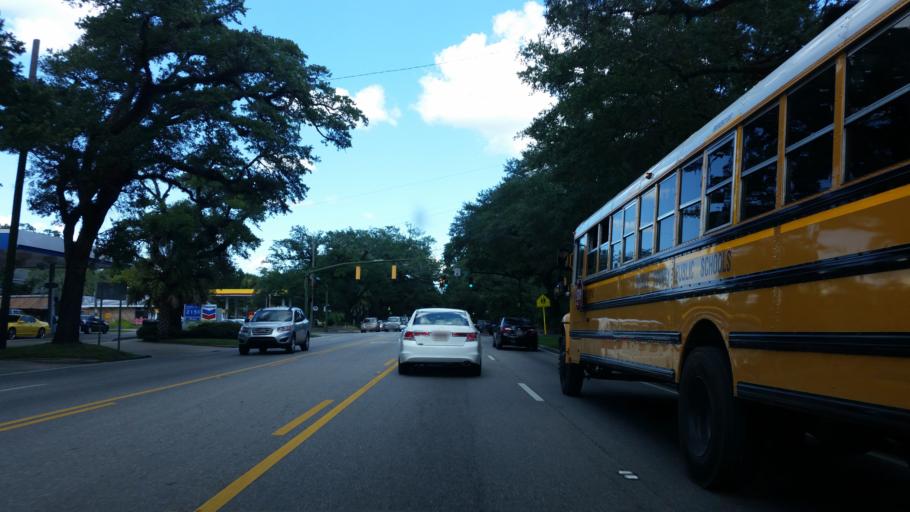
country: US
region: Alabama
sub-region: Mobile County
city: Mobile
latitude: 30.6821
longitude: -88.0670
